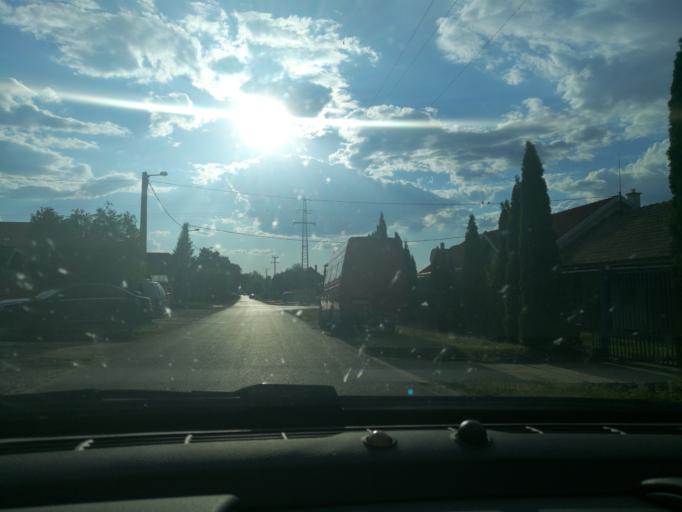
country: HU
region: Szabolcs-Szatmar-Bereg
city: Nyirpazony
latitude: 47.9459
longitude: 21.7802
